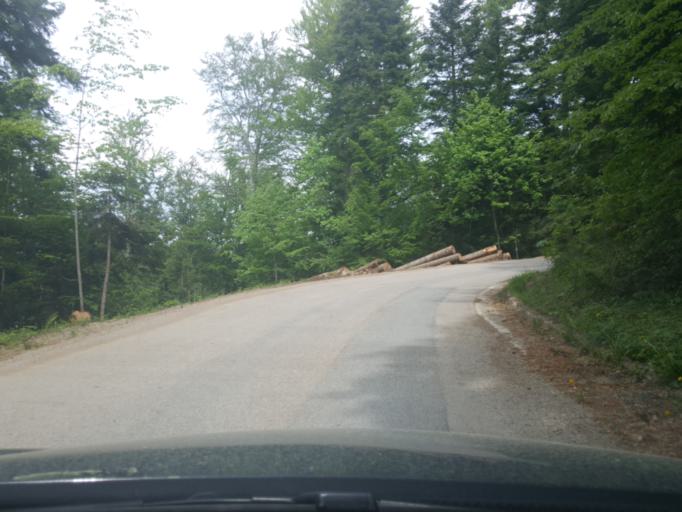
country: RS
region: Central Serbia
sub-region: Zlatiborski Okrug
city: Bajina Basta
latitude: 43.8919
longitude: 19.5274
